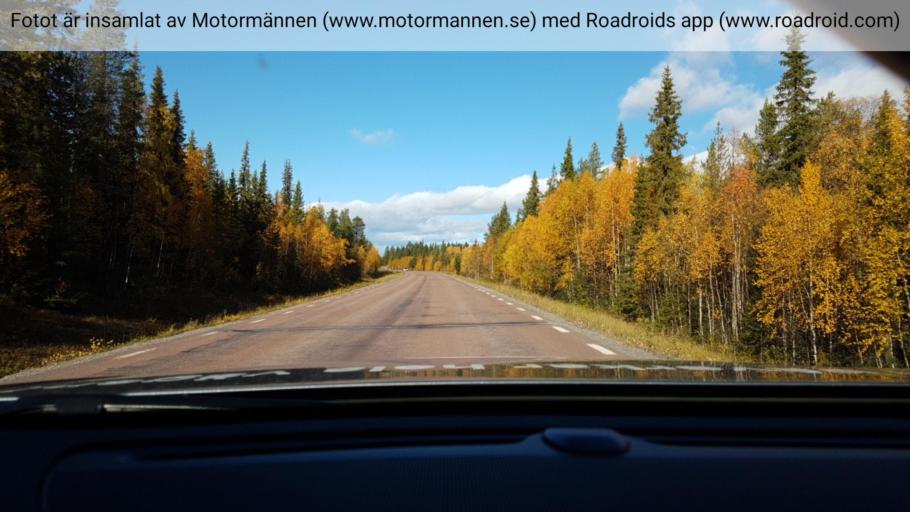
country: SE
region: Norrbotten
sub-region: Arjeplogs Kommun
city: Arjeplog
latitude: 65.9870
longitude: 18.1900
